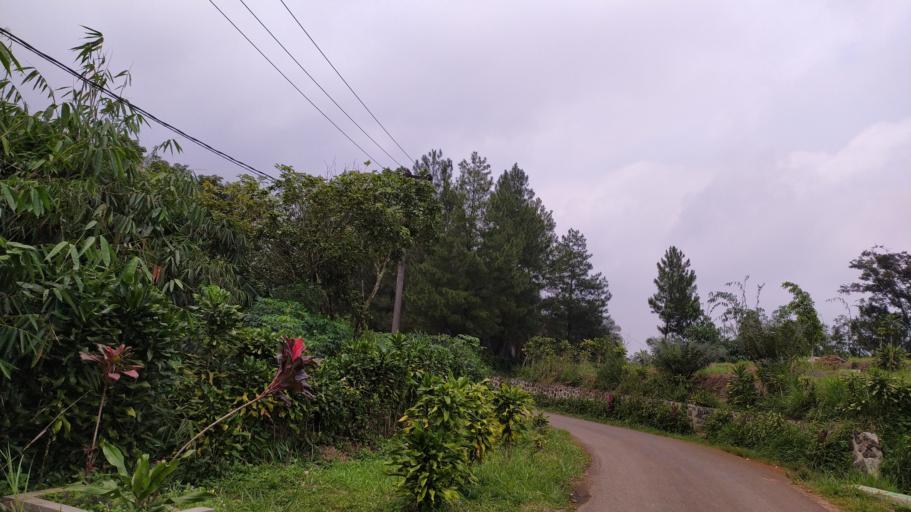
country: ID
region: West Java
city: Ciampea
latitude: -6.6285
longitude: 106.7074
